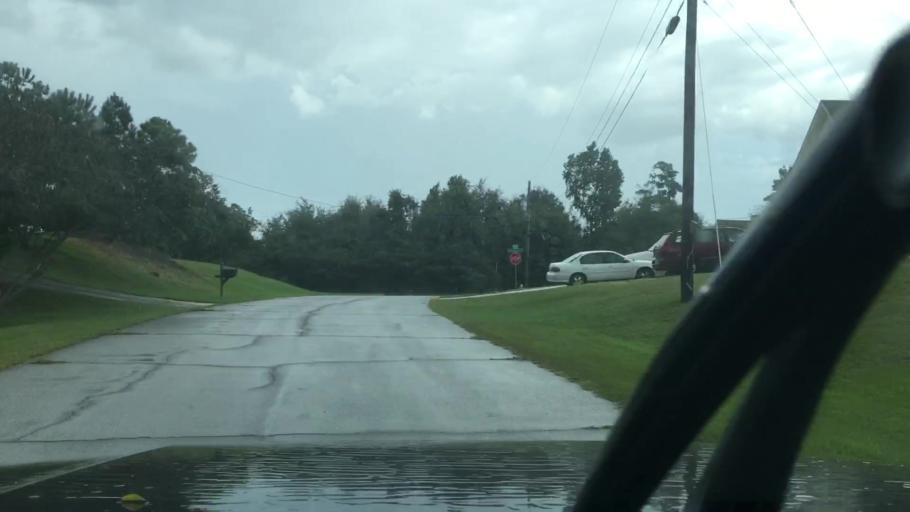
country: US
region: Georgia
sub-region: Bibb County
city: West Point
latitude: 32.8168
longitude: -83.7943
